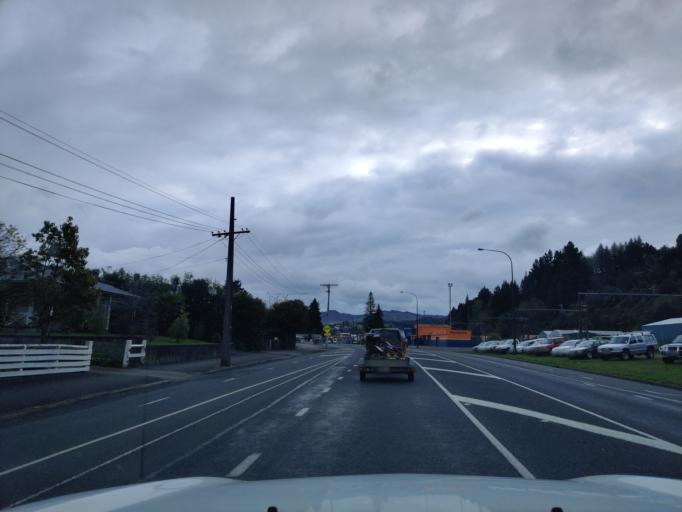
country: NZ
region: Waikato
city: Turangi
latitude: -38.8824
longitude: 175.2730
